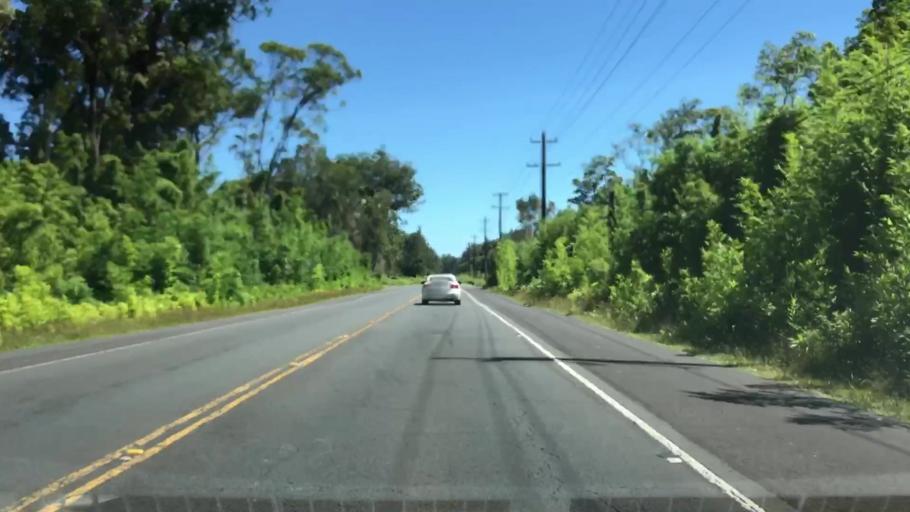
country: US
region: Hawaii
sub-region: Hawaii County
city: Fern Acres
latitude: 19.4868
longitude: -155.1524
